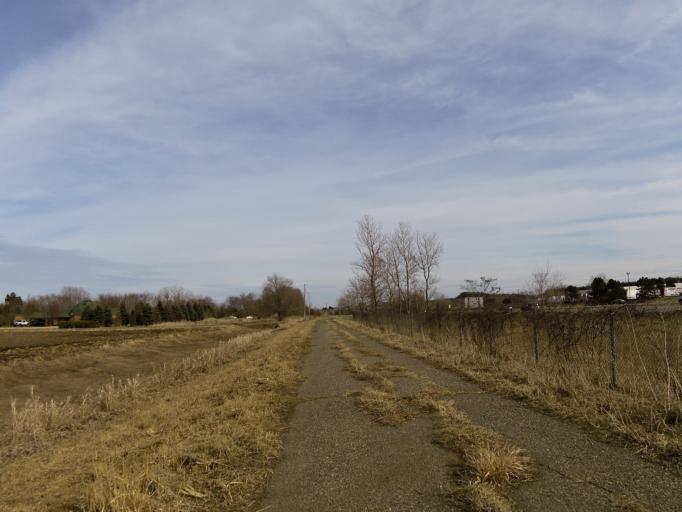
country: US
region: Minnesota
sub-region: Washington County
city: Lake Elmo
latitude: 44.9492
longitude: -92.8517
